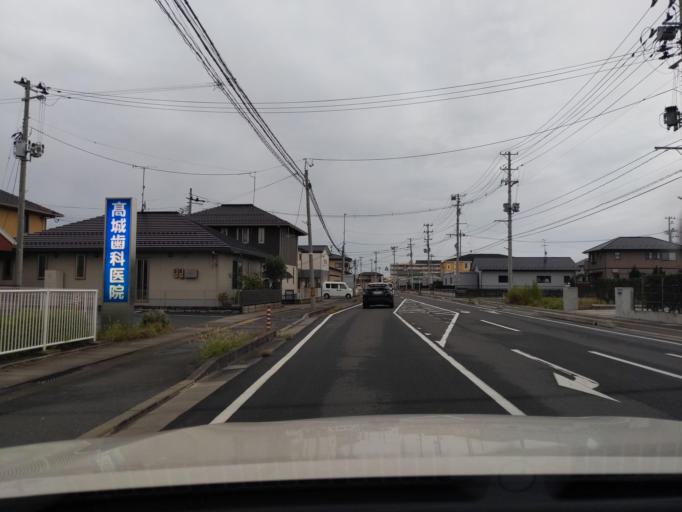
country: JP
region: Miyagi
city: Ishinomaki
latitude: 38.4404
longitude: 141.2640
